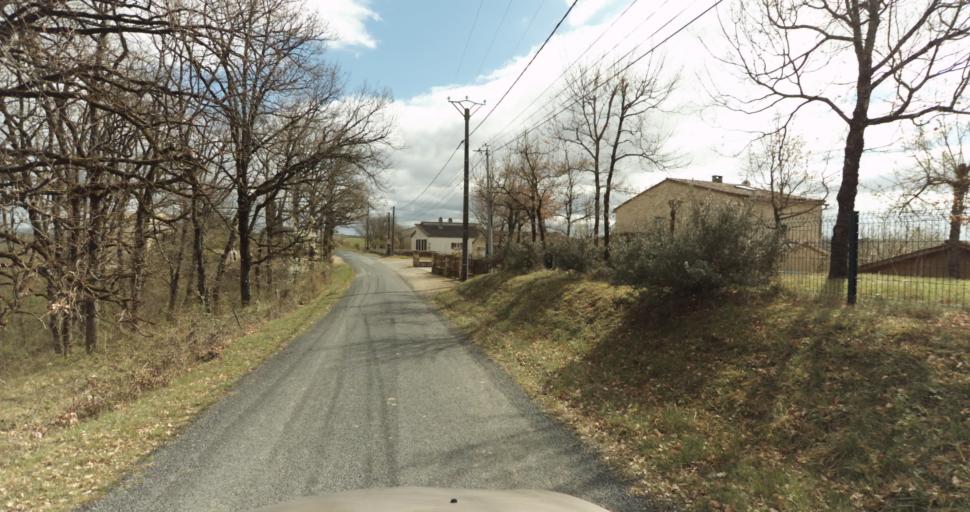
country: FR
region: Midi-Pyrenees
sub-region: Departement du Tarn
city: Puygouzon
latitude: 43.8832
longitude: 2.1515
